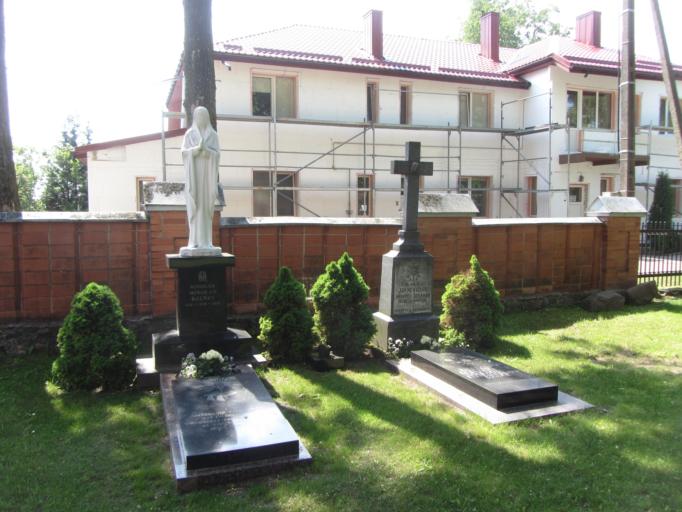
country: LT
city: Kaisiadorys
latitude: 54.8604
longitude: 24.4573
